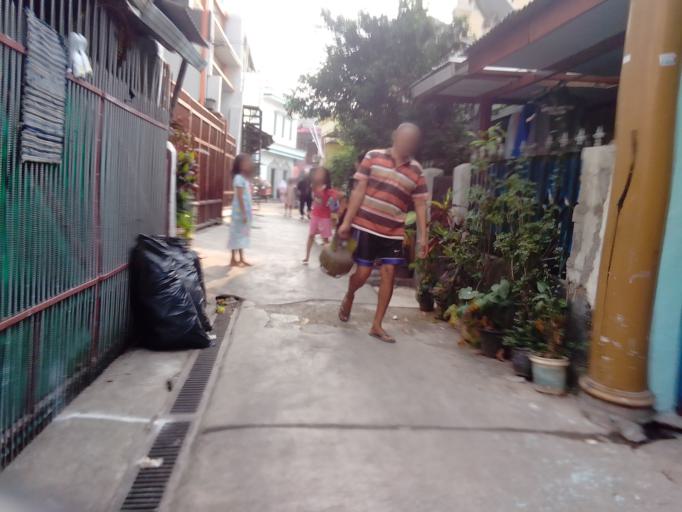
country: ID
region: Jakarta Raya
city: Jakarta
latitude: -6.1982
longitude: 106.8126
